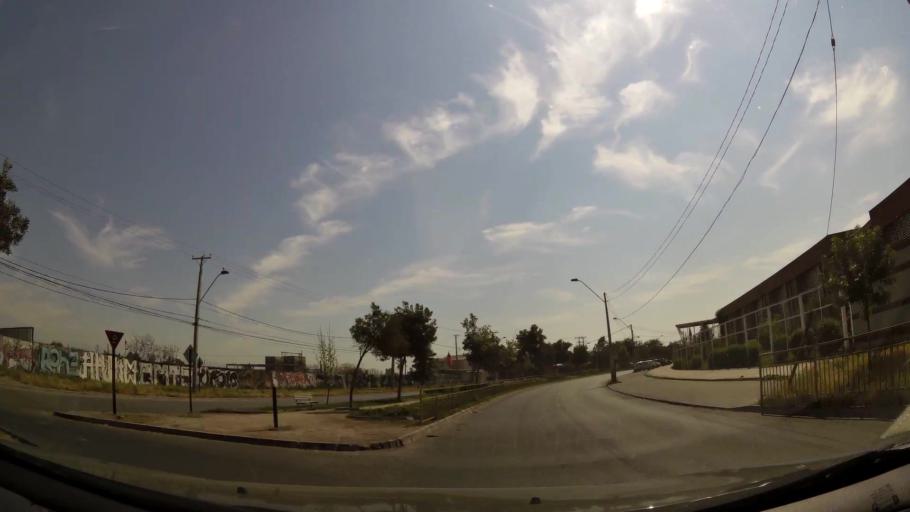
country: CL
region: Santiago Metropolitan
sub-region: Provincia de Santiago
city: La Pintana
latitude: -33.5723
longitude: -70.5994
